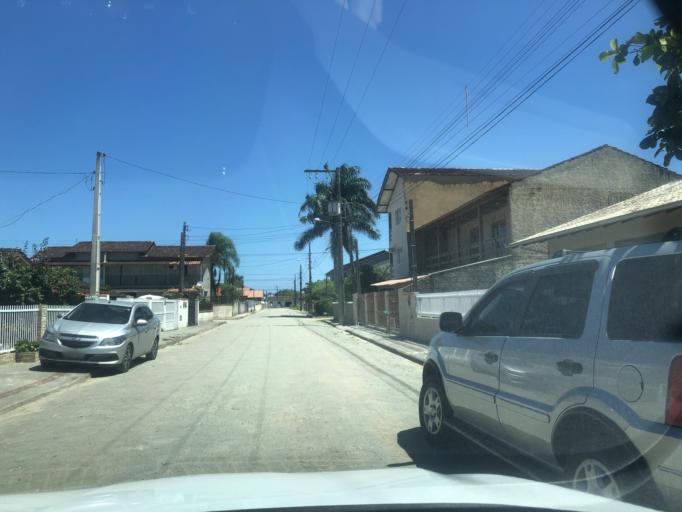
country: BR
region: Santa Catarina
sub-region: Sao Francisco Do Sul
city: Sao Francisco do Sul
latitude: -26.2278
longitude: -48.5240
